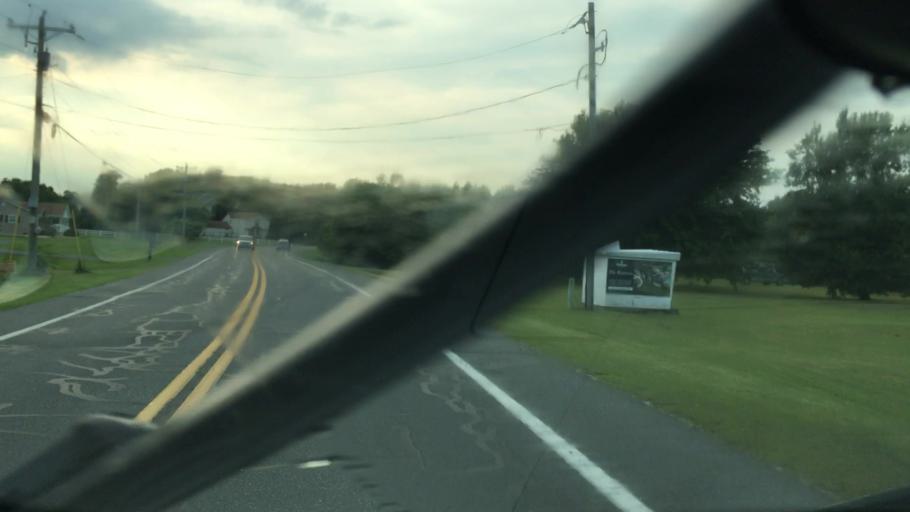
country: US
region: Delaware
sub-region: Sussex County
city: Ocean View
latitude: 38.5290
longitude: -75.0842
